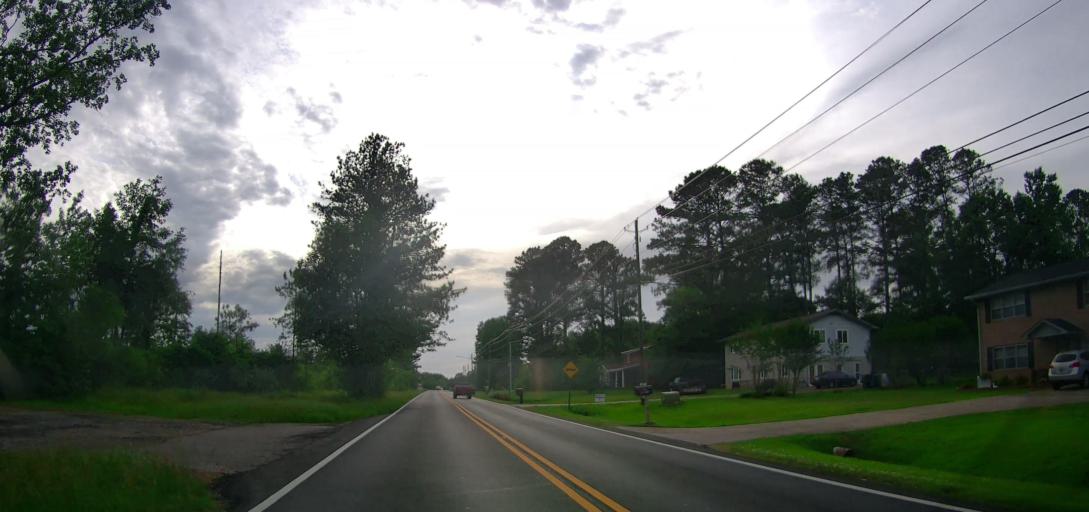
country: US
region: Alabama
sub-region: Calhoun County
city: Oxford
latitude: 33.5856
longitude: -85.7953
